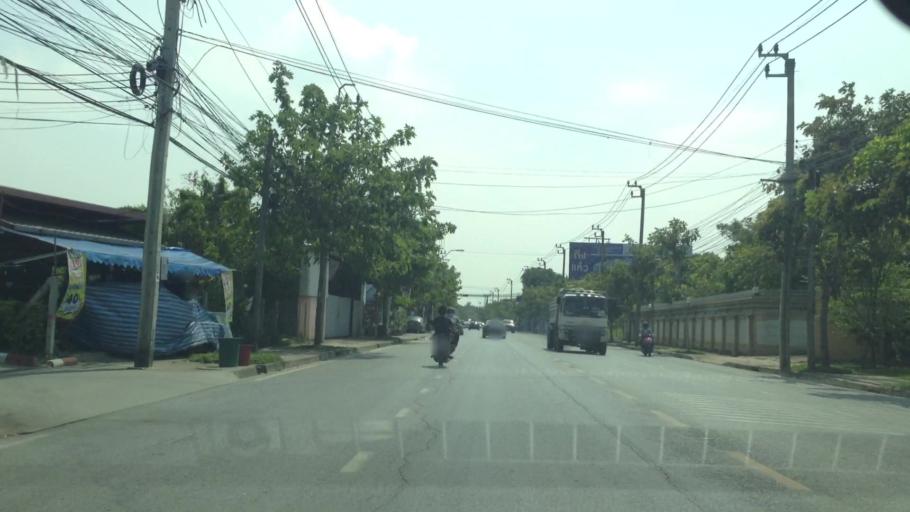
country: TH
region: Bangkok
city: Bang Khen
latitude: 13.8913
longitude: 100.6418
